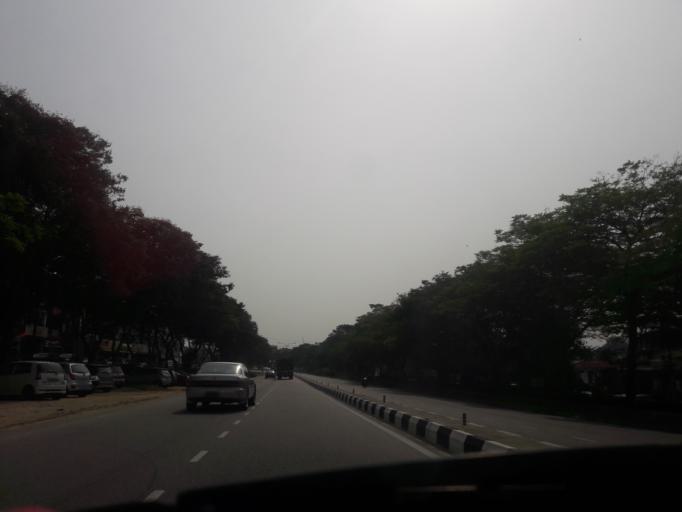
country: MY
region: Kedah
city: Kulim
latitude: 5.3768
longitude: 100.5404
